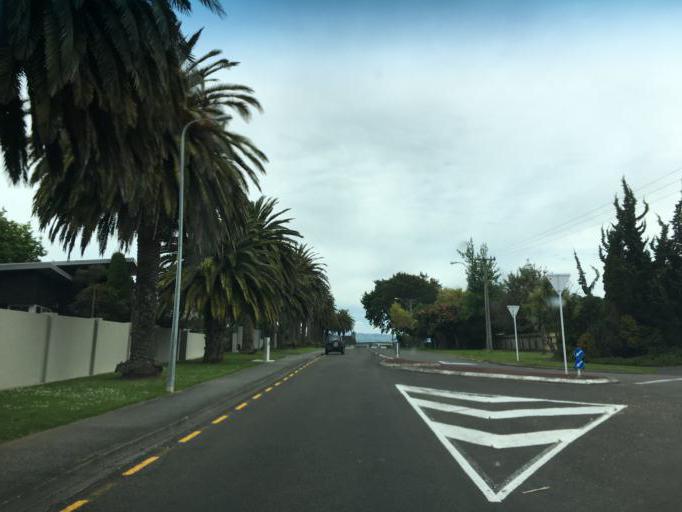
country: NZ
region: Manawatu-Wanganui
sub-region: Palmerston North City
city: Palmerston North
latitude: -40.3776
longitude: 175.5787
